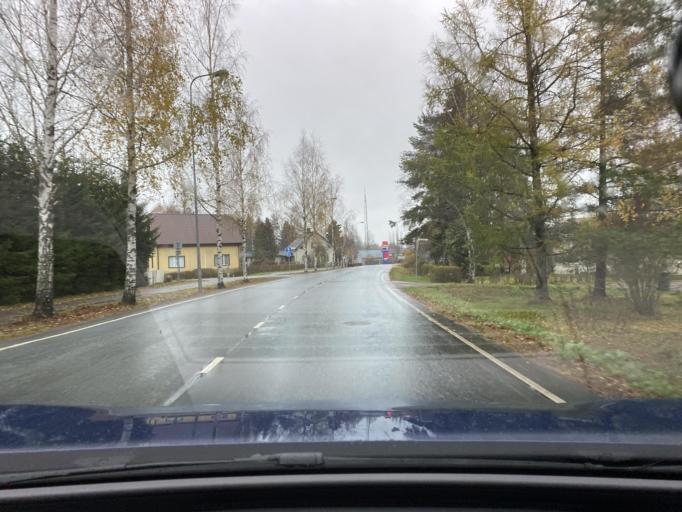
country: FI
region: Varsinais-Suomi
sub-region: Loimaa
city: Alastaro
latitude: 60.9480
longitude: 22.8646
